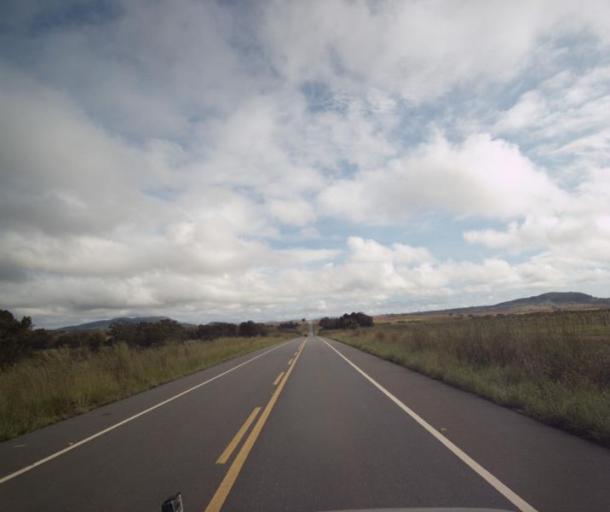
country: BR
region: Goias
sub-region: Barro Alto
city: Barro Alto
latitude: -15.2862
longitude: -48.6794
